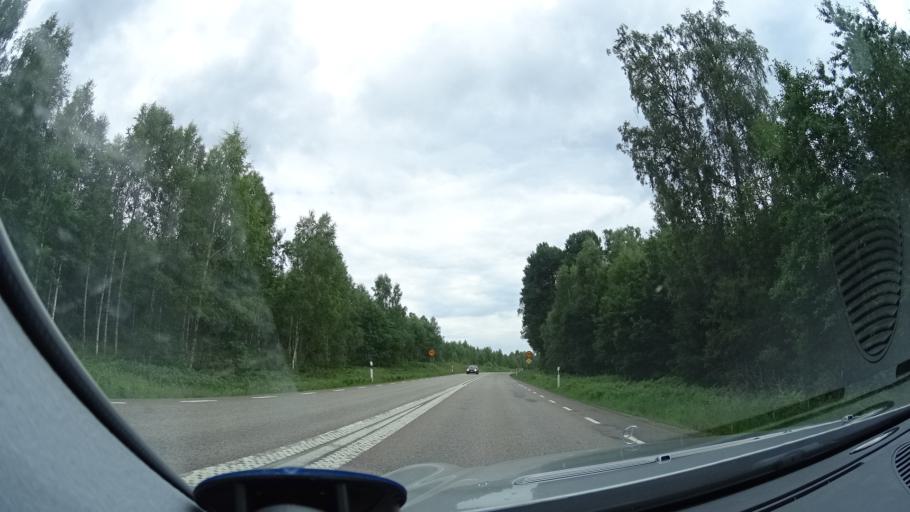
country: SE
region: Kronoberg
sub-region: Tingsryds Kommun
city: Tingsryd
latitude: 56.5141
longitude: 14.9917
